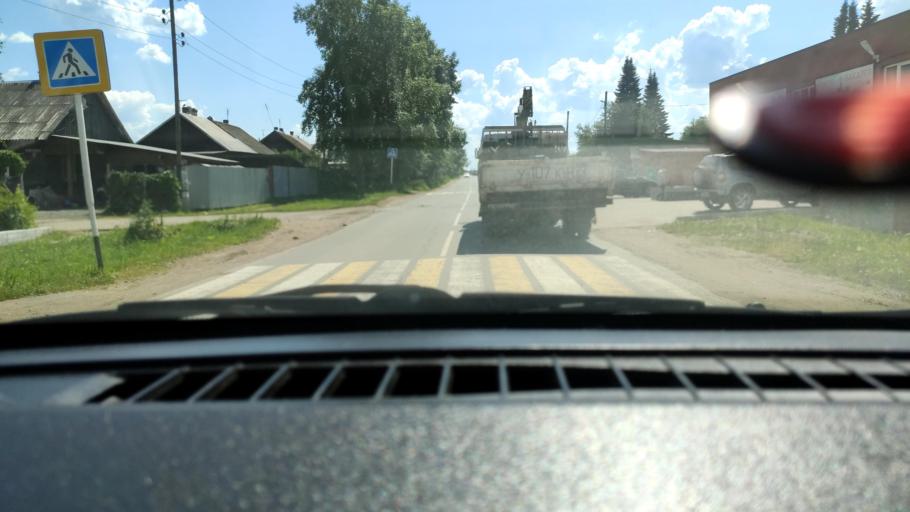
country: RU
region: Perm
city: Sylva
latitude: 58.0329
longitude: 56.7595
